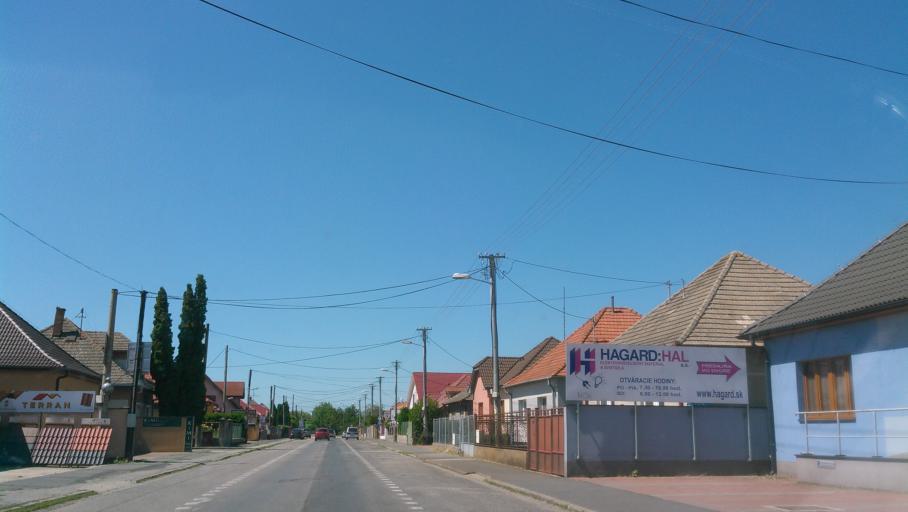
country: SK
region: Nitriansky
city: Sellye
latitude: 48.1545
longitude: 17.8700
